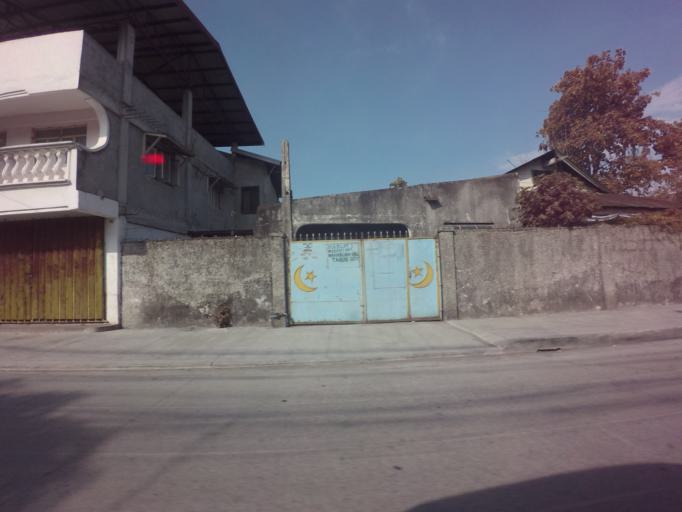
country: PH
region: Calabarzon
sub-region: Province of Rizal
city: Taguig
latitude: 14.4991
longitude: 121.0532
